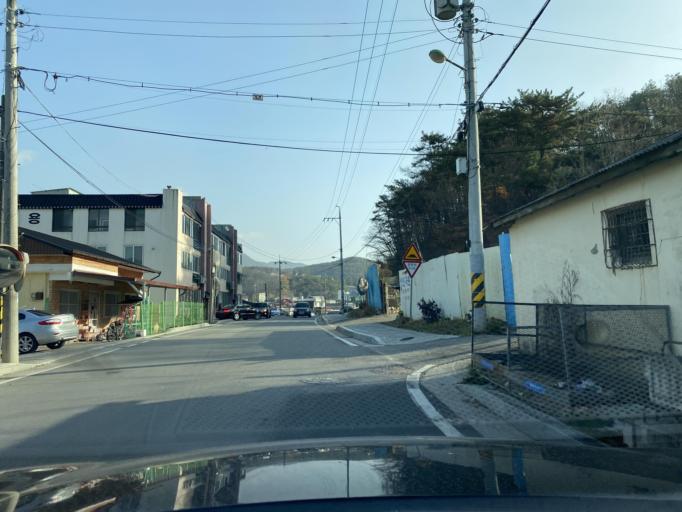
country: KR
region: Chungcheongnam-do
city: Yesan
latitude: 36.6793
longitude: 126.8293
